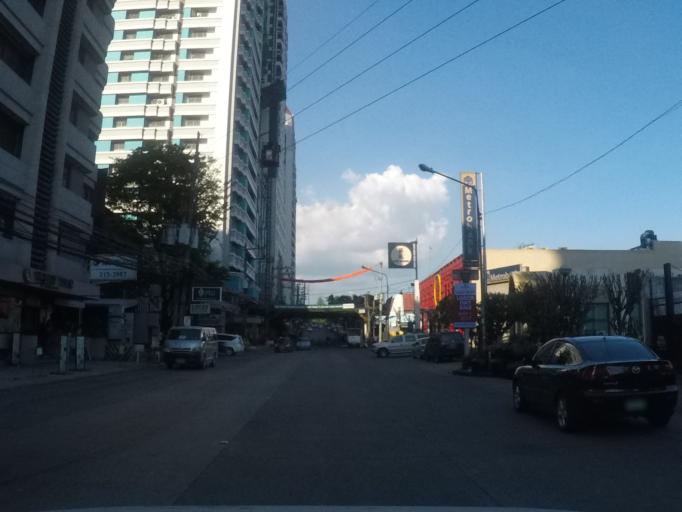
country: PH
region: Metro Manila
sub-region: Pasig
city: Pasig City
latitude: 14.6050
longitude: 121.0543
